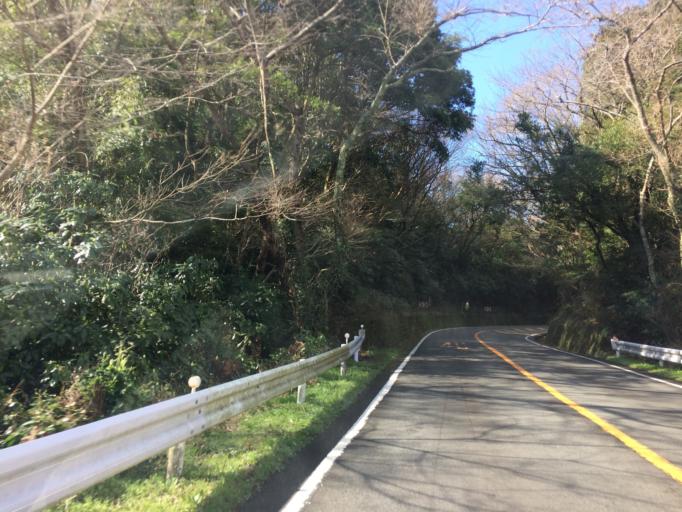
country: JP
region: Shizuoka
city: Shizuoka-shi
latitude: 34.9644
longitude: 138.4507
